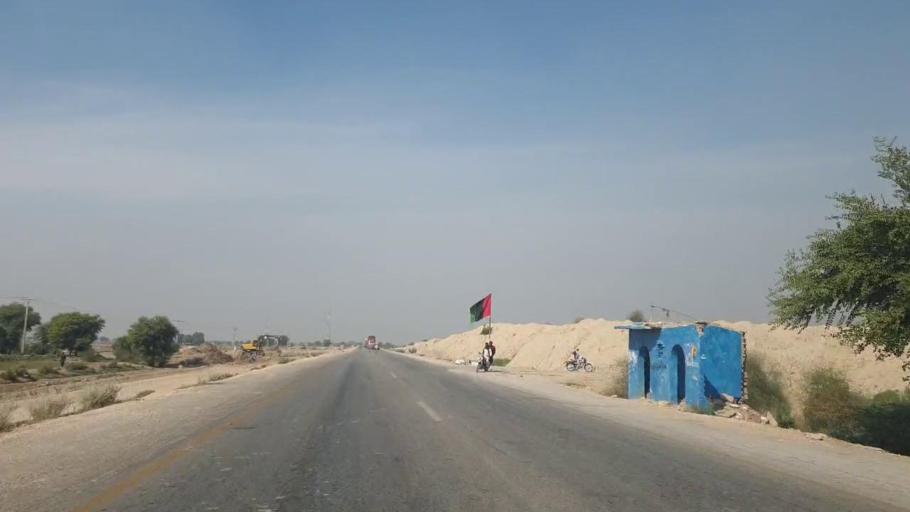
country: PK
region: Sindh
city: Sann
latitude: 25.9731
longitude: 68.1873
